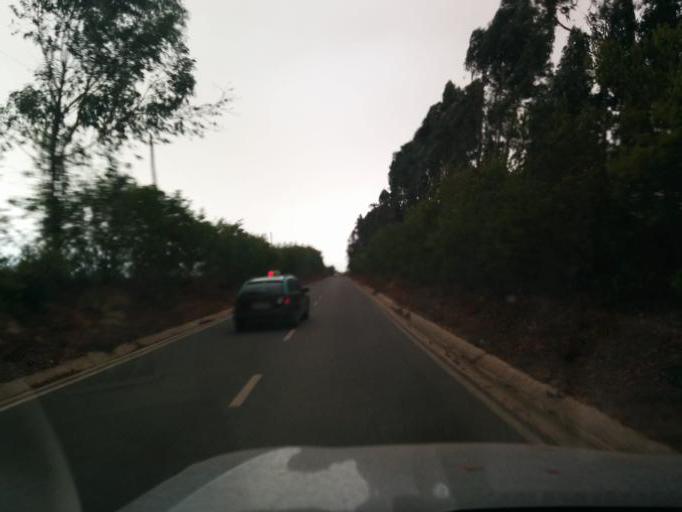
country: PT
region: Beja
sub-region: Odemira
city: Sao Teotonio
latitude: 37.5417
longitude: -8.7494
